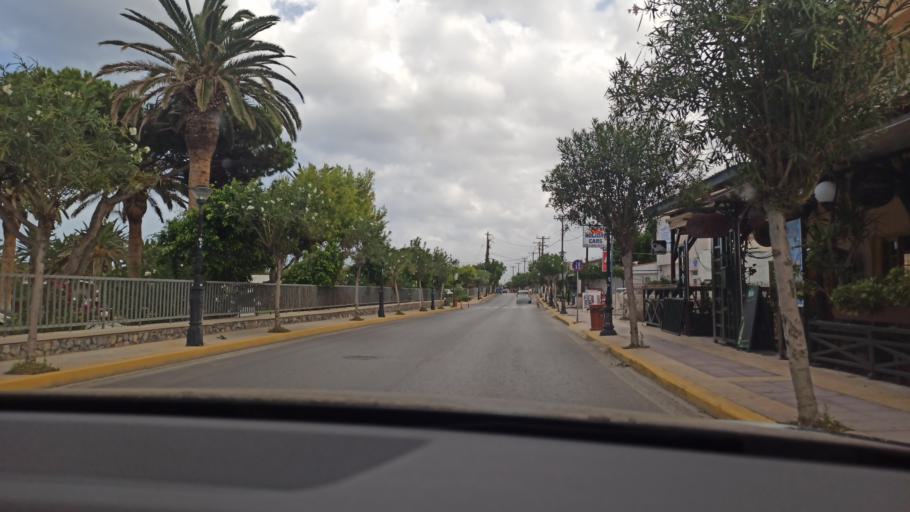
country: GR
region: Crete
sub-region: Nomos Irakleiou
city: Gazi
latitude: 35.3359
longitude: 25.0797
